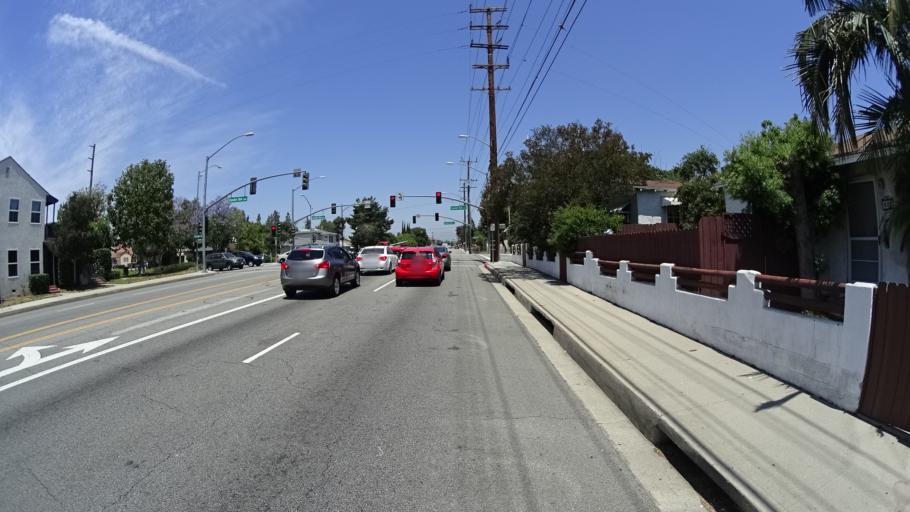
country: US
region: California
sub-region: Los Angeles County
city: Burbank
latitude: 34.1750
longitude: -118.3362
